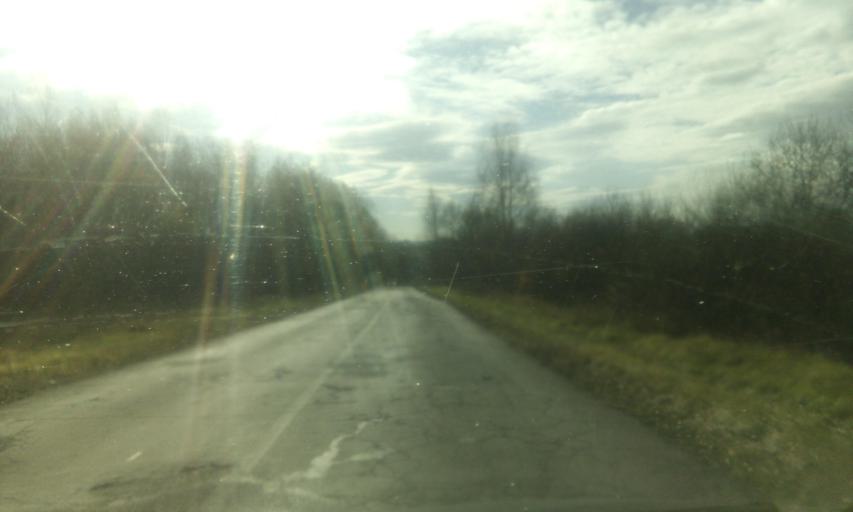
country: RU
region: Tula
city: Dubovka
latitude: 53.9517
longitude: 38.0292
